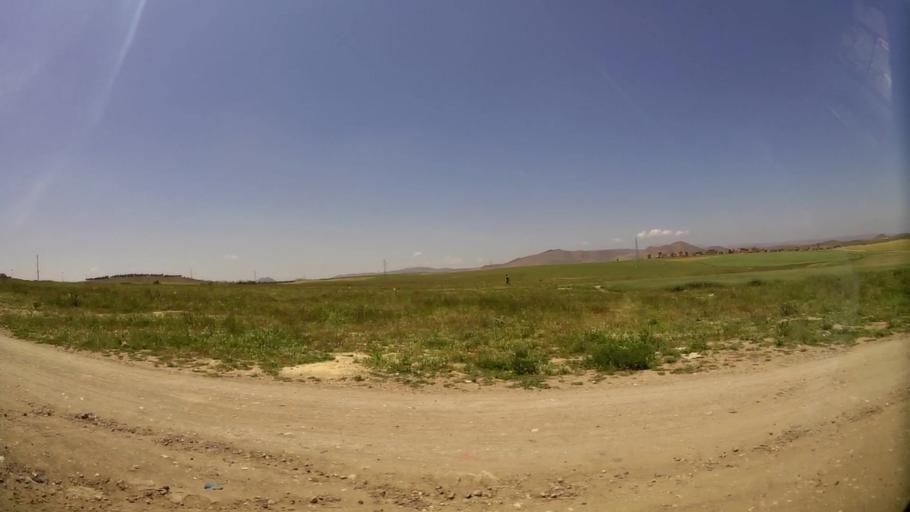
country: MA
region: Oriental
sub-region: Oujda-Angad
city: Oujda
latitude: 34.6868
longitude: -1.9561
